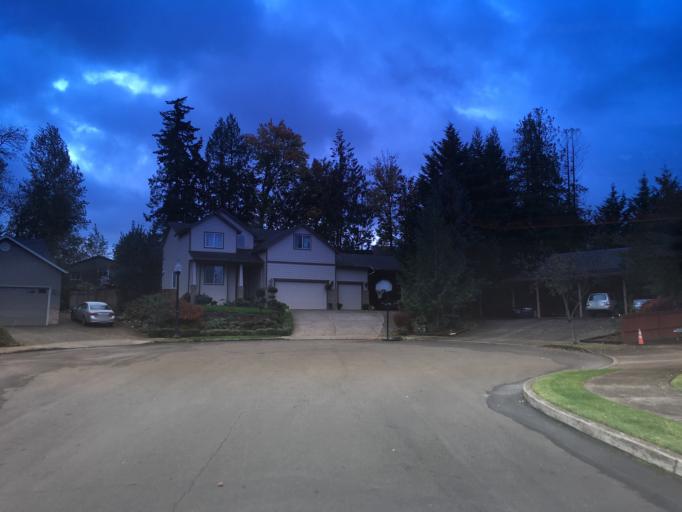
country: US
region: Oregon
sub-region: Multnomah County
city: Fairview
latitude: 45.5383
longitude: -122.4274
